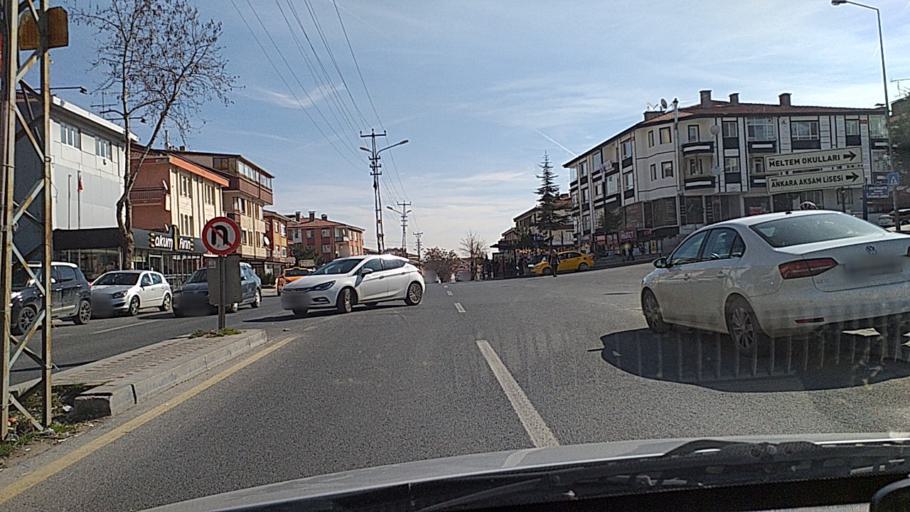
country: TR
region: Ankara
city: Ankara
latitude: 39.9845
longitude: 32.8269
